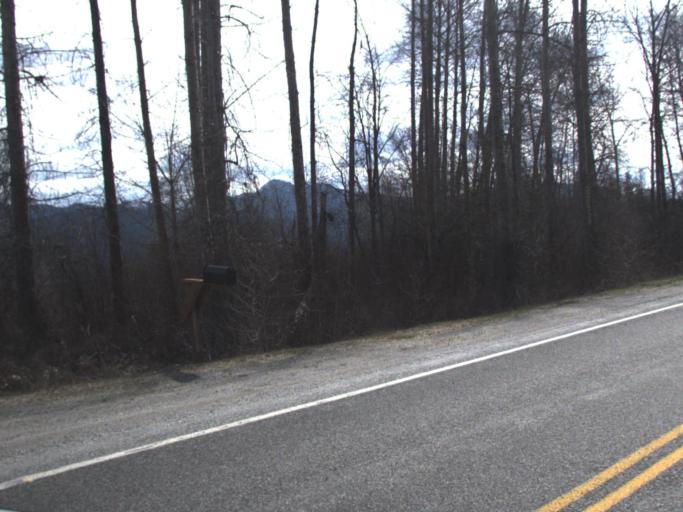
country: US
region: Washington
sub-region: Pend Oreille County
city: Newport
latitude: 48.4254
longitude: -117.3167
